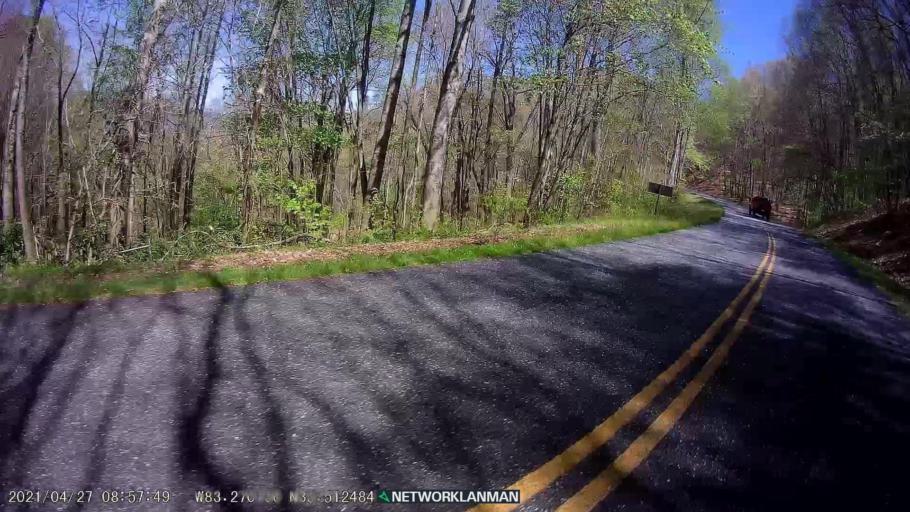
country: US
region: North Carolina
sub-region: Swain County
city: Cherokee
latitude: 35.5125
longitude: -83.2707
